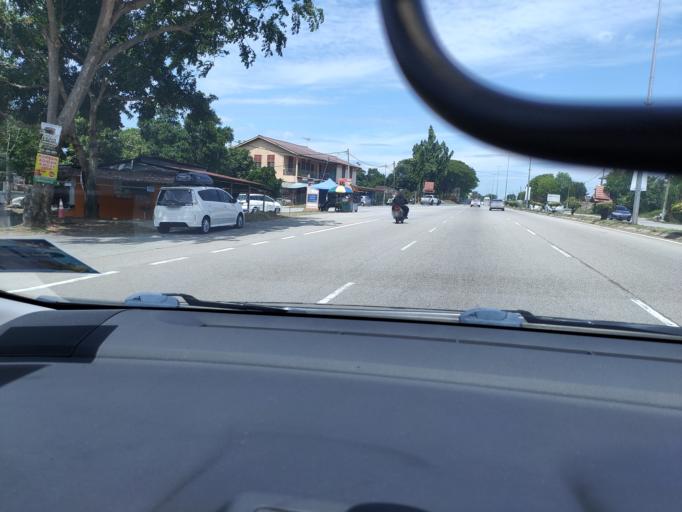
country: MY
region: Melaka
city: Batu Berendam
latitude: 2.2638
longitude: 102.2191
